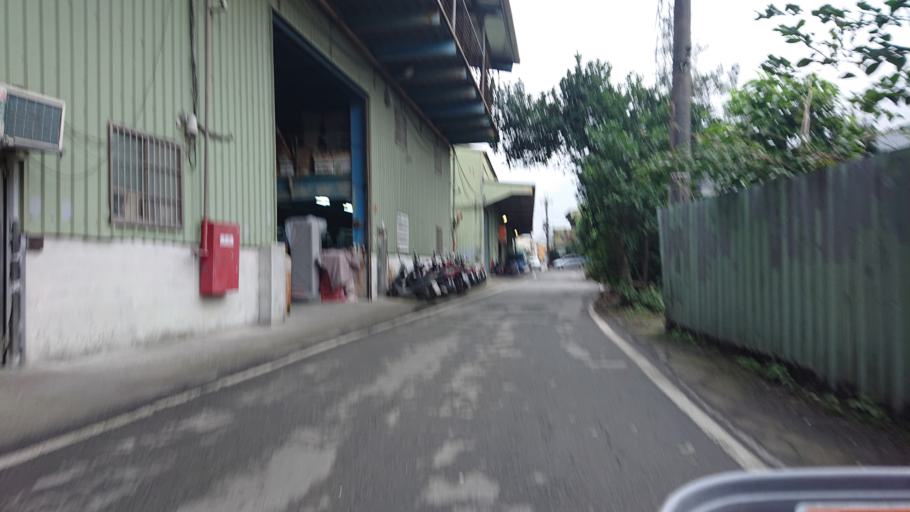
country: TW
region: Taiwan
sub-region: Taoyuan
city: Taoyuan
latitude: 24.9431
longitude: 121.3935
